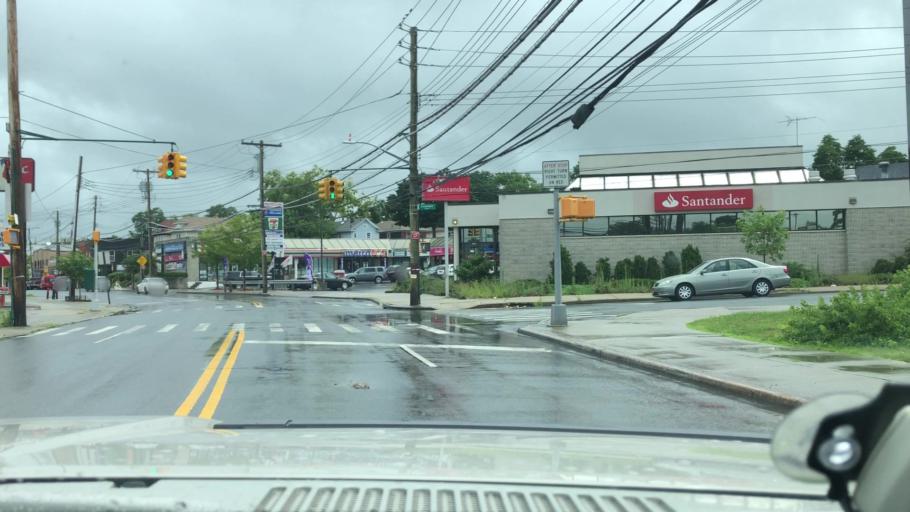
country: US
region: New York
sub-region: Richmond County
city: Bloomfield
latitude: 40.6242
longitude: -74.1376
